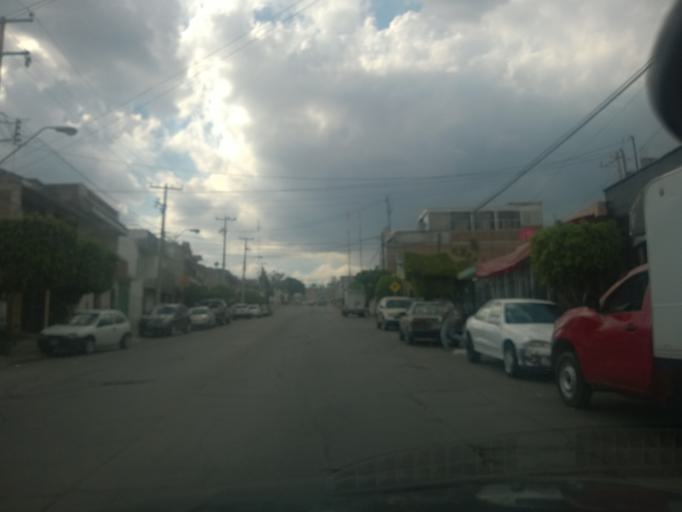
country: MX
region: Guanajuato
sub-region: Leon
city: Ejido la Joya
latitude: 21.1282
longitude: -101.7161
